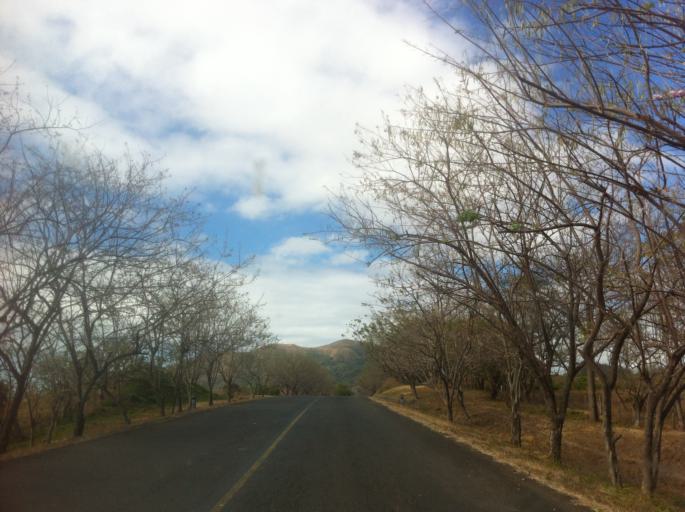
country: NI
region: Chontales
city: Acoyapa
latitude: 12.0024
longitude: -85.1854
